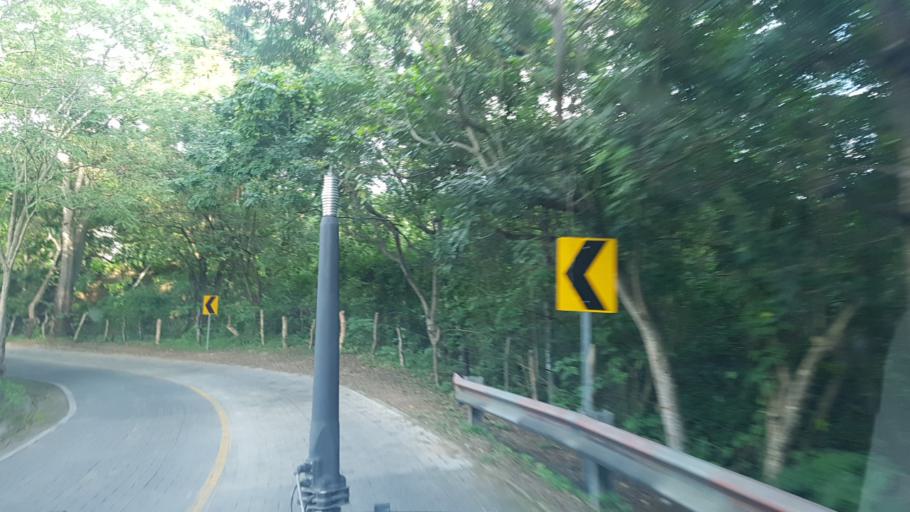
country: NI
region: Nueva Segovia
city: Ocotal
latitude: 13.6433
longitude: -86.5955
